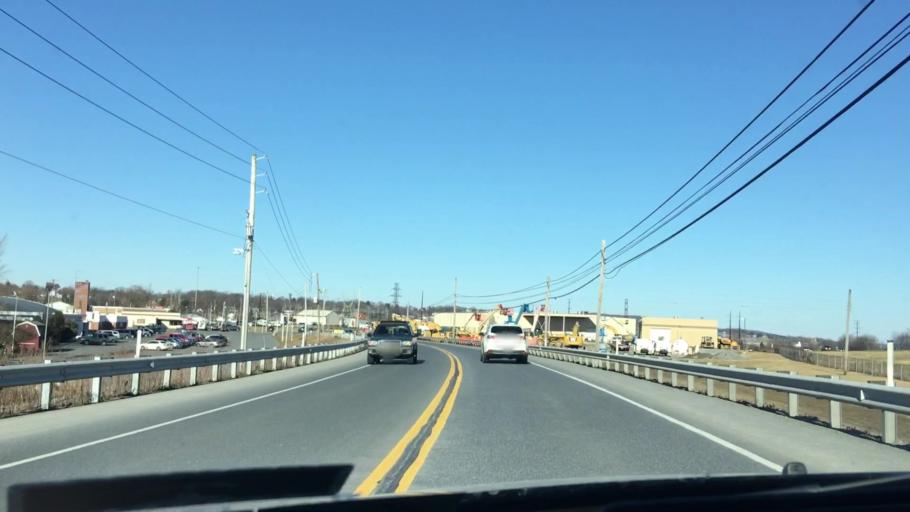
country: US
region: Pennsylvania
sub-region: Lancaster County
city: Brownstown
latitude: 40.1339
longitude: -76.2128
